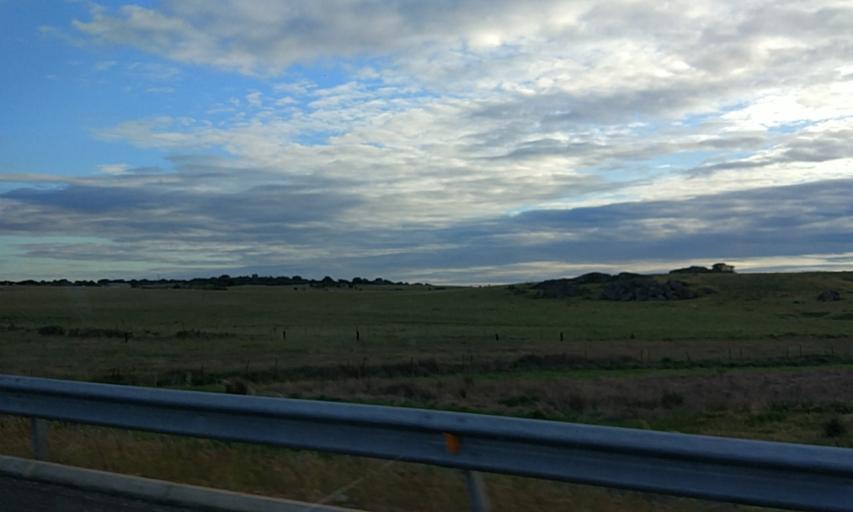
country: ES
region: Extremadura
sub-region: Provincia de Caceres
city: Caceres
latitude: 39.4693
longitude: -6.4244
